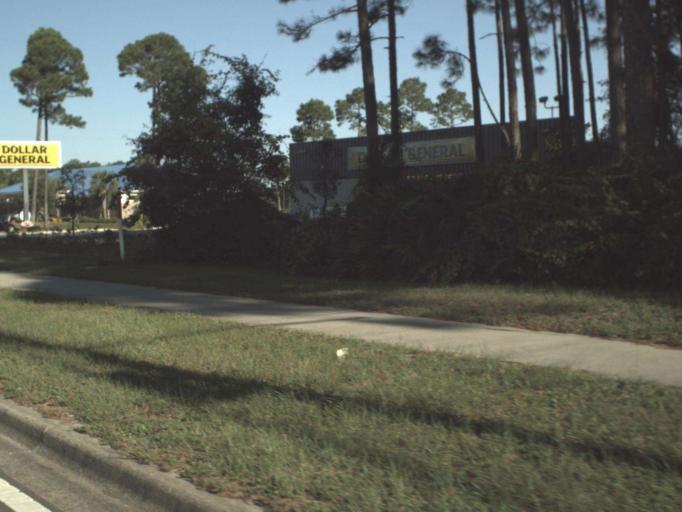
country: US
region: Florida
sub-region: Bay County
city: Panama City Beach
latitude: 30.1960
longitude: -85.8296
